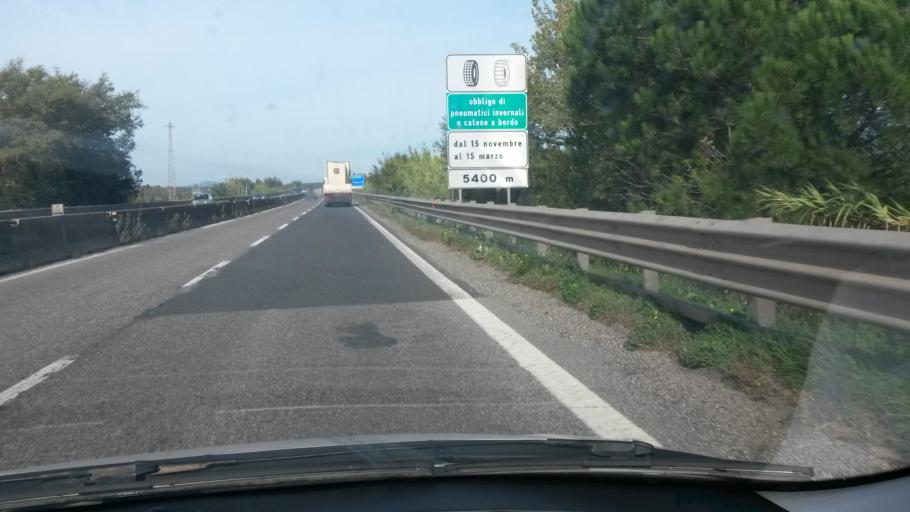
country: IT
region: Tuscany
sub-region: Provincia di Livorno
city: S.P. in Palazzi
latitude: 43.3250
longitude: 10.5300
